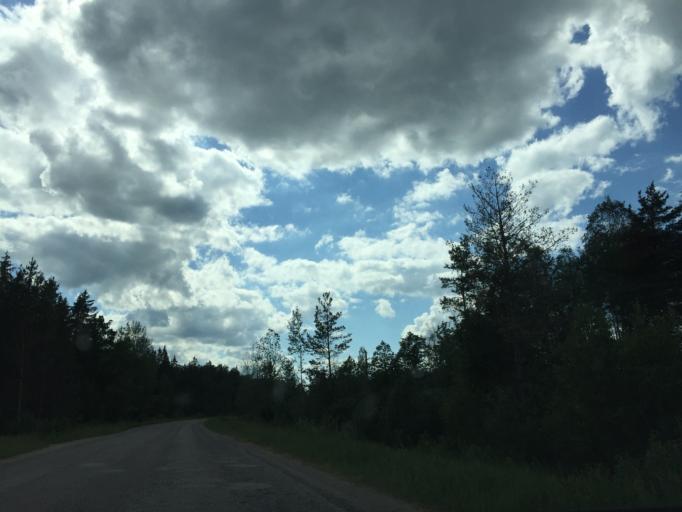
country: LV
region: Tukuma Rajons
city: Tukums
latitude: 56.9120
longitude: 23.1843
